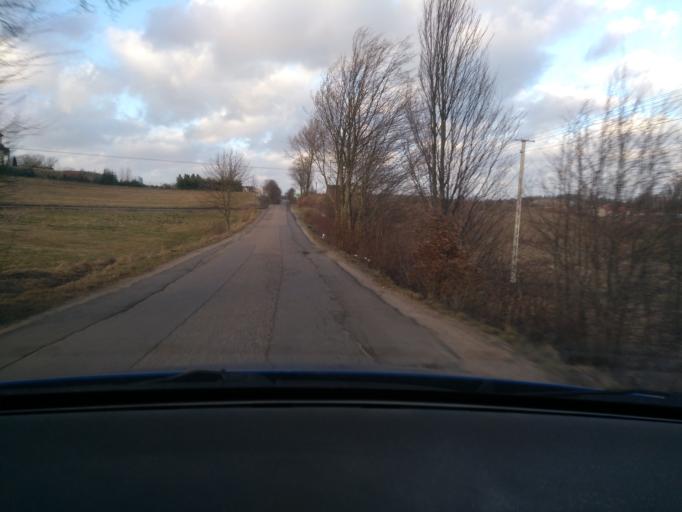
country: PL
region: Pomeranian Voivodeship
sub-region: Powiat kartuski
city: Kartuzy
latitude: 54.3792
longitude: 18.2171
